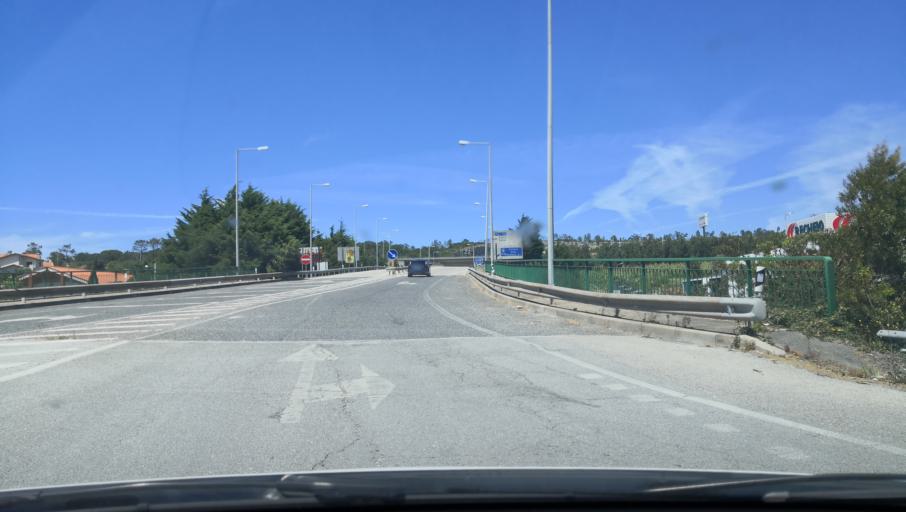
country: PT
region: Coimbra
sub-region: Figueira da Foz
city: Tavarede
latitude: 40.1472
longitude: -8.8326
